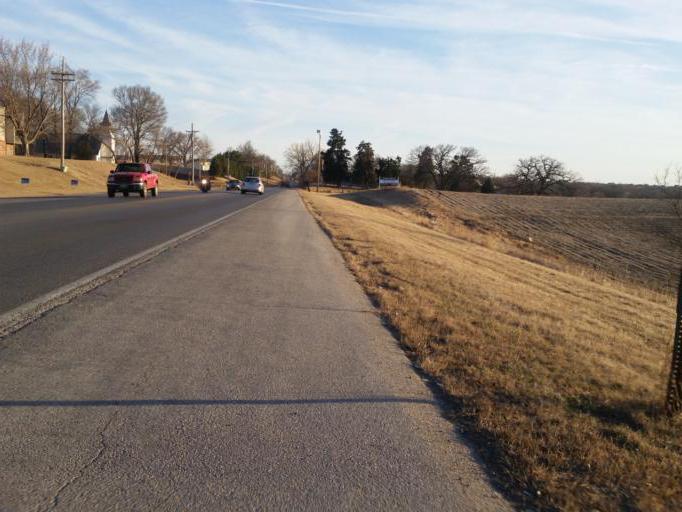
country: US
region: Nebraska
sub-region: Sarpy County
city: Offutt Air Force Base
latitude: 41.1309
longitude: -95.9666
